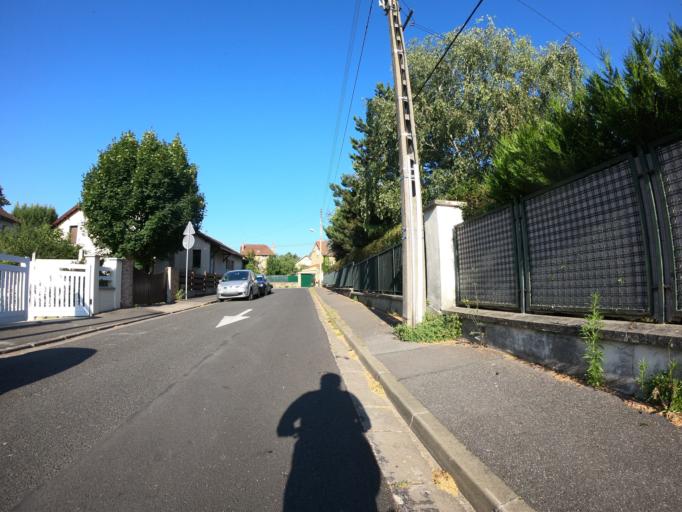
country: FR
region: Ile-de-France
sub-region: Departement de l'Essonne
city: Verrieres-le-Buisson
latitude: 48.7435
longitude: 2.2730
